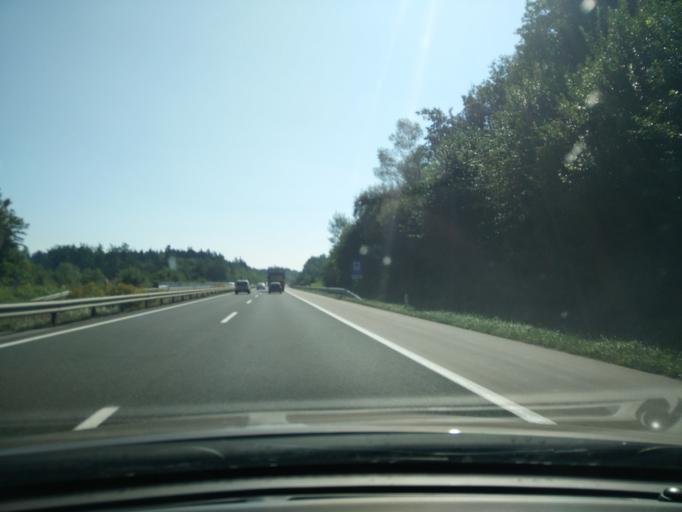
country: SI
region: Kranj
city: Kokrica
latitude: 46.2604
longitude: 14.3648
